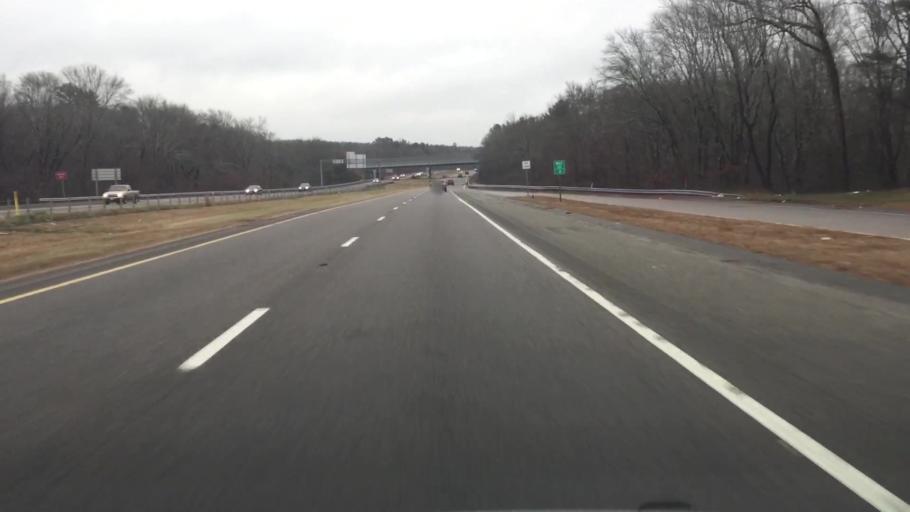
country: US
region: Massachusetts
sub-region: Plymouth County
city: Middleborough Center
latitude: 41.8707
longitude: -70.8934
